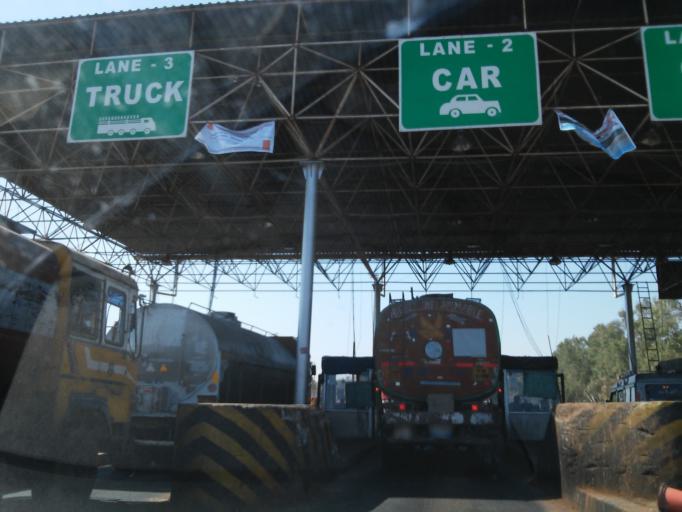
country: IN
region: Gujarat
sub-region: Sabar Kantha
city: Modasa
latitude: 23.6165
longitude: 73.2557
